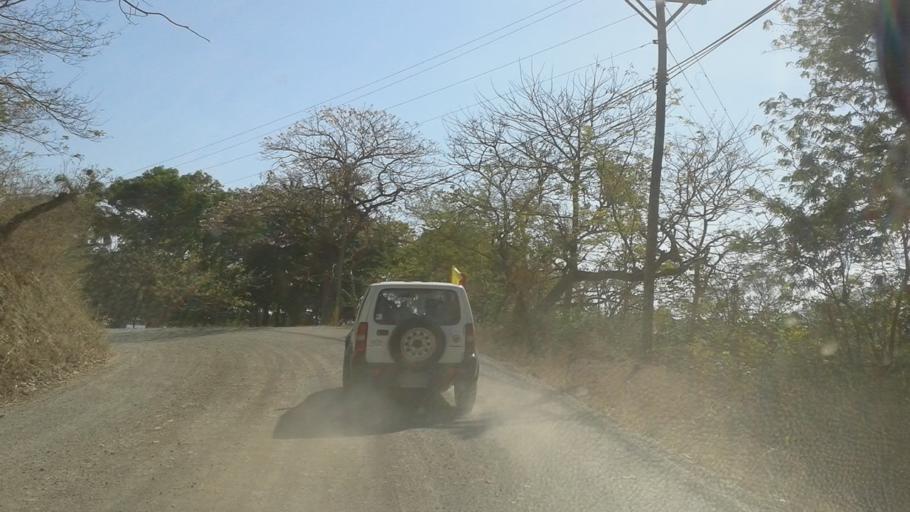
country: CR
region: Guanacaste
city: Santa Cruz
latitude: 10.1220
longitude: -85.7940
